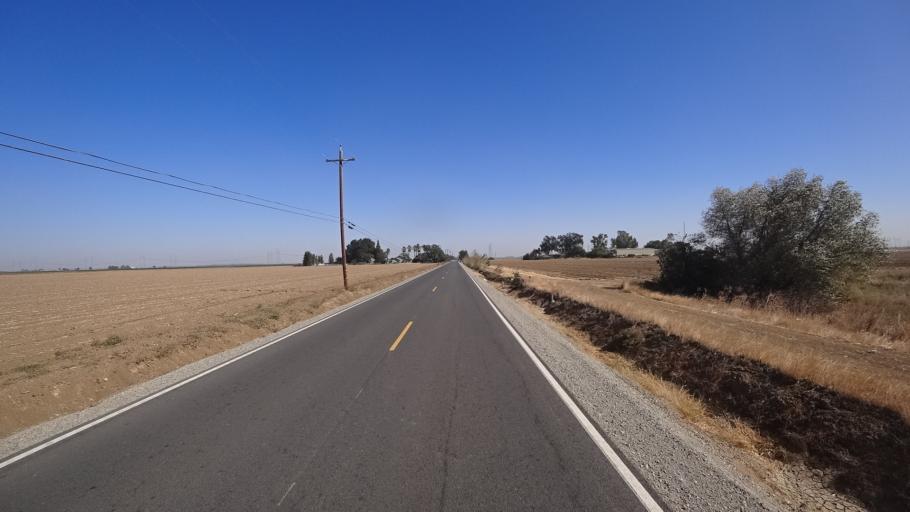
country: US
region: California
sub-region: Yolo County
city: Winters
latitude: 38.5839
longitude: -121.9385
